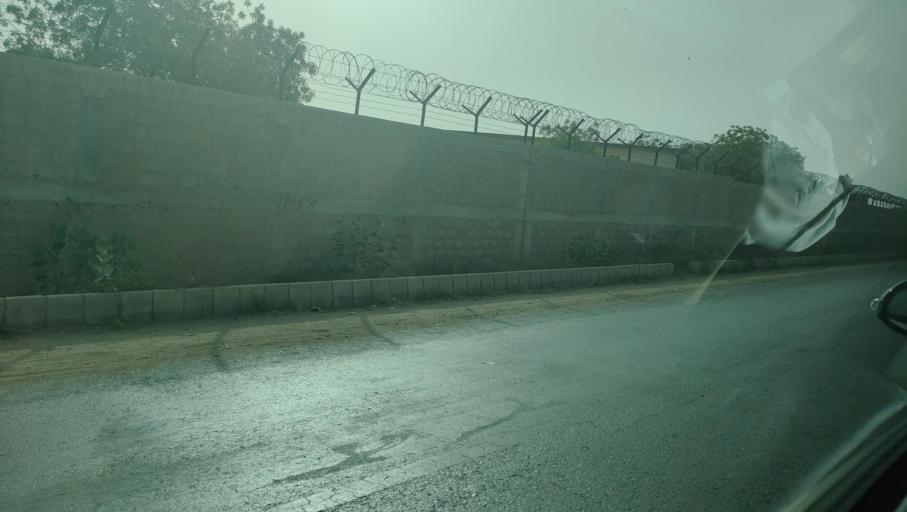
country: PK
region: Sindh
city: Malir Cantonment
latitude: 24.9171
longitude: 67.1875
